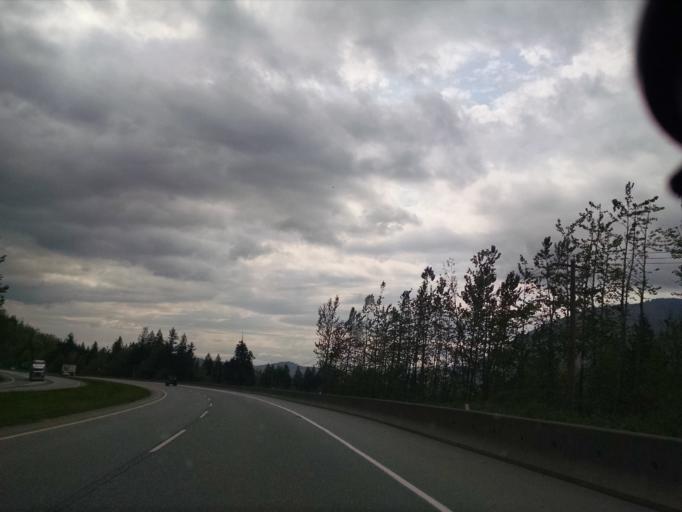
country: CA
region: British Columbia
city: Agassiz
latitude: 49.2997
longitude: -121.6517
